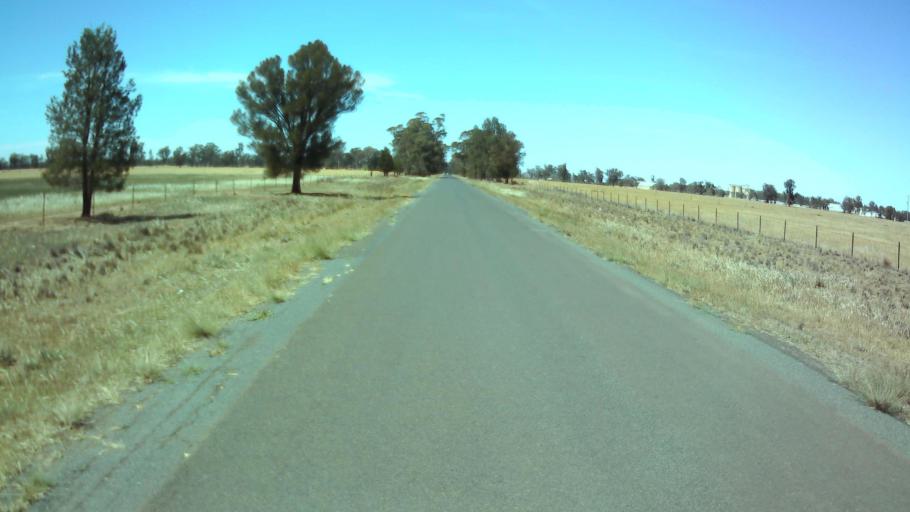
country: AU
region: New South Wales
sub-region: Weddin
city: Grenfell
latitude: -34.1068
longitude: 147.8865
